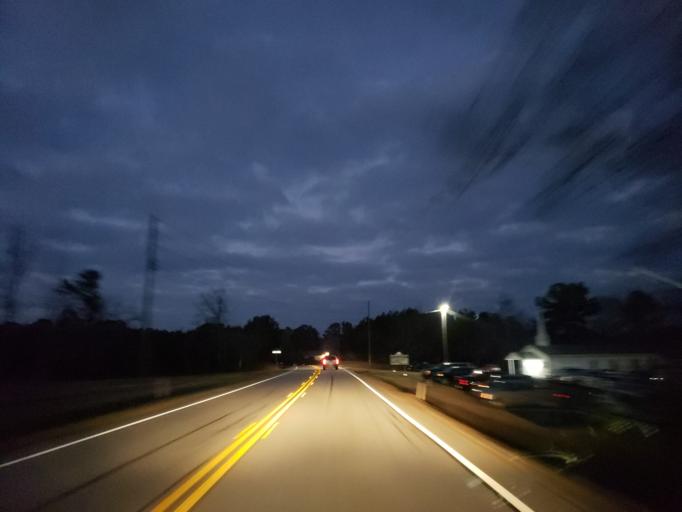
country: US
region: Georgia
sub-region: Polk County
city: Rockmart
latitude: 33.9016
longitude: -84.9962
